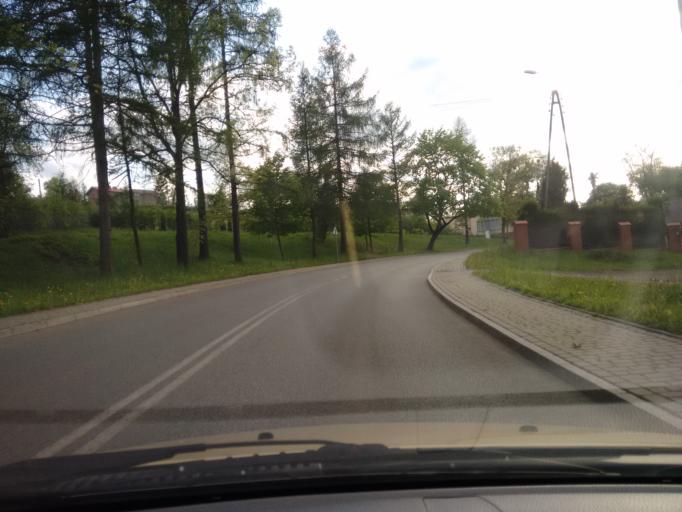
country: PL
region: Silesian Voivodeship
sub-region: Powiat cieszynski
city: Cieszyn
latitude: 49.7504
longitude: 18.6602
